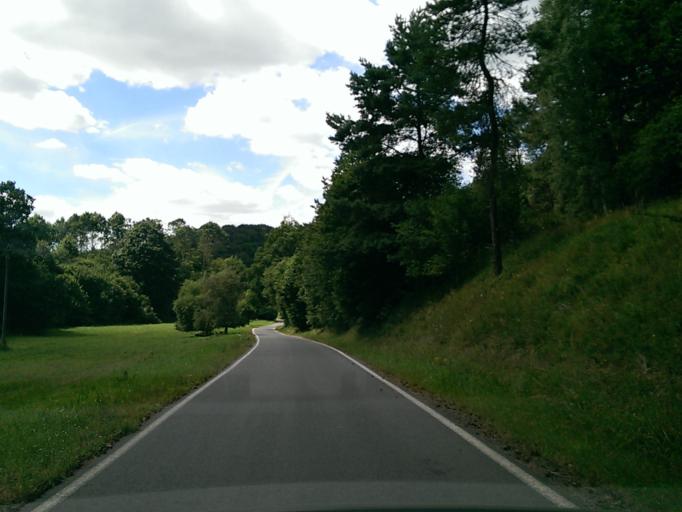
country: CZ
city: Duba
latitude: 50.4712
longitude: 14.5136
